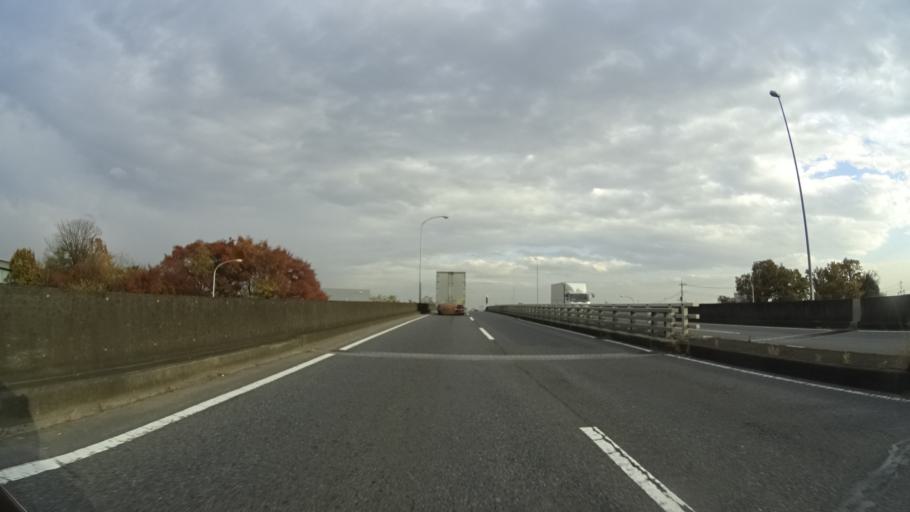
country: JP
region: Gunma
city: Isesaki
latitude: 36.3552
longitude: 139.2118
